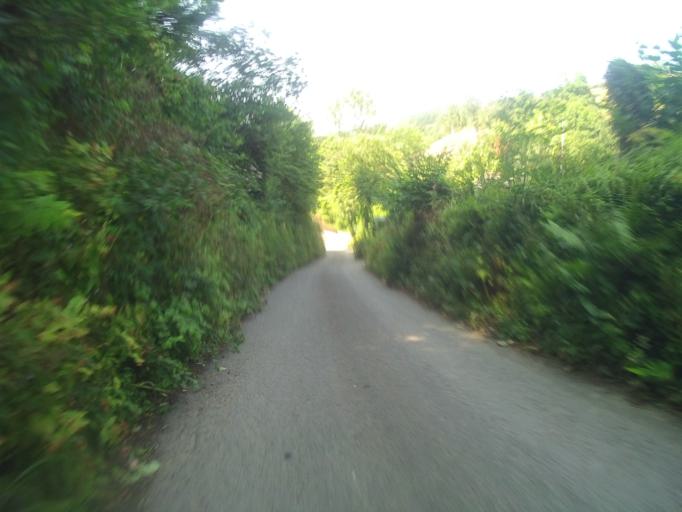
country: GB
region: England
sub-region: Devon
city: Dartmouth
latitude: 50.3558
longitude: -3.6012
